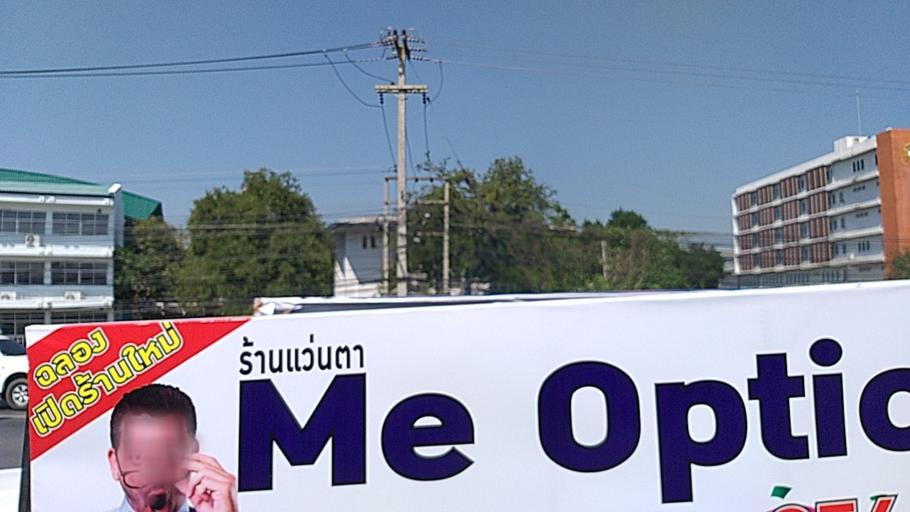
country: TH
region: Nakhon Ratchasima
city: Nakhon Ratchasima
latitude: 14.9841
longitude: 102.0929
